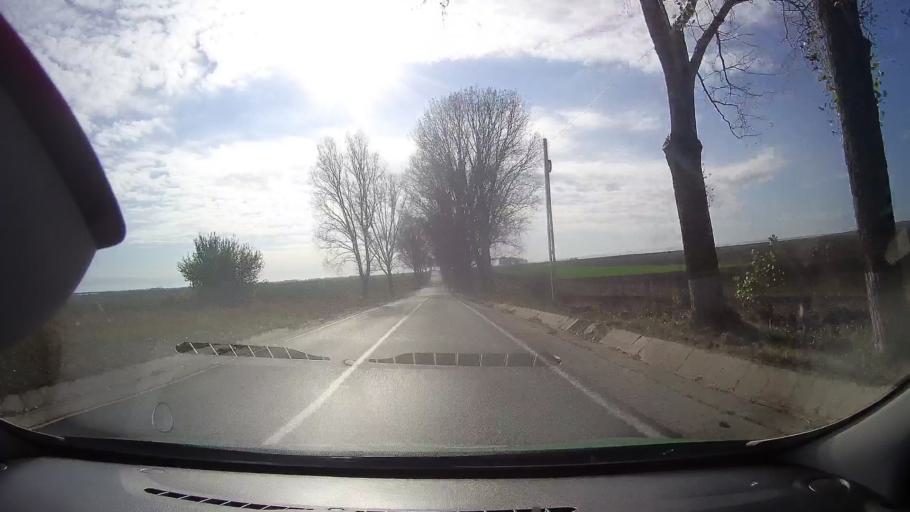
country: RO
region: Tulcea
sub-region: Comuna Valea Nucarilor
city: Agighiol
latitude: 45.0030
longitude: 28.8856
